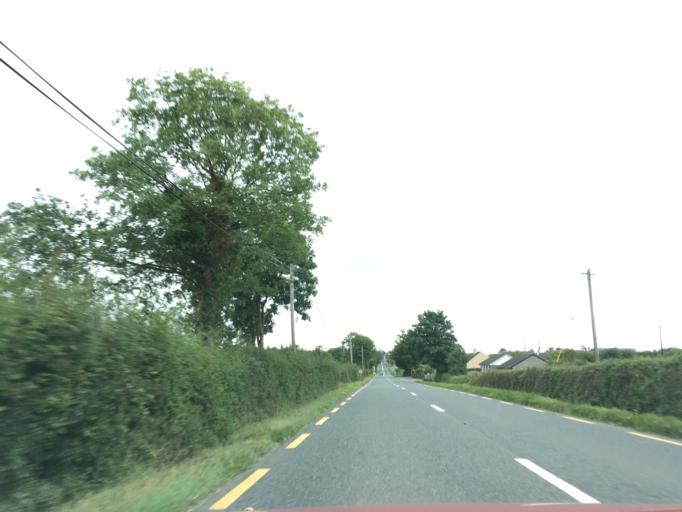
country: IE
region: Munster
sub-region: South Tipperary
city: Cluain Meala
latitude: 52.4165
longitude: -7.7604
